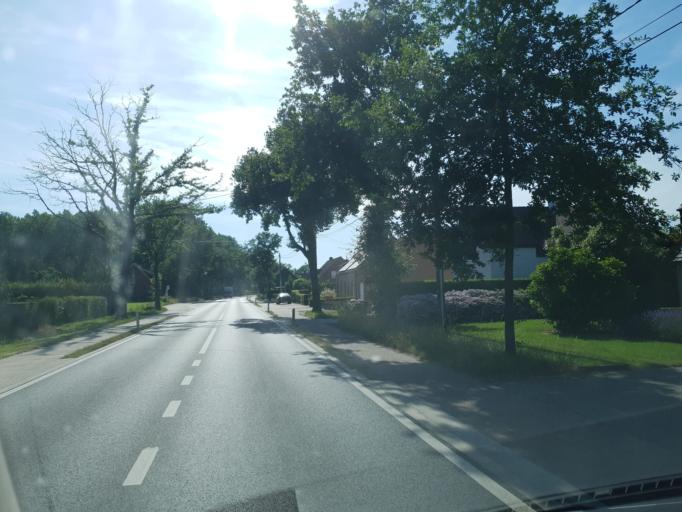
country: BE
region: Flanders
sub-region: Provincie Antwerpen
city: Rijkevorsel
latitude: 51.3477
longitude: 4.7097
